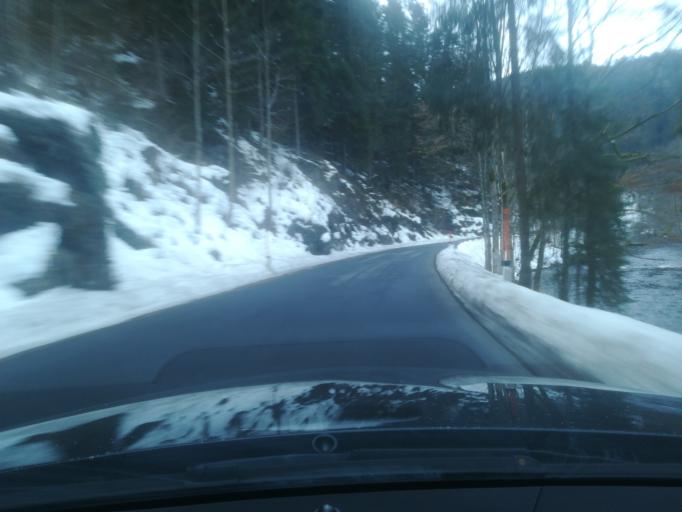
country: AT
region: Upper Austria
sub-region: Politischer Bezirk Perg
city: Perg
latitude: 48.4111
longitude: 14.6375
